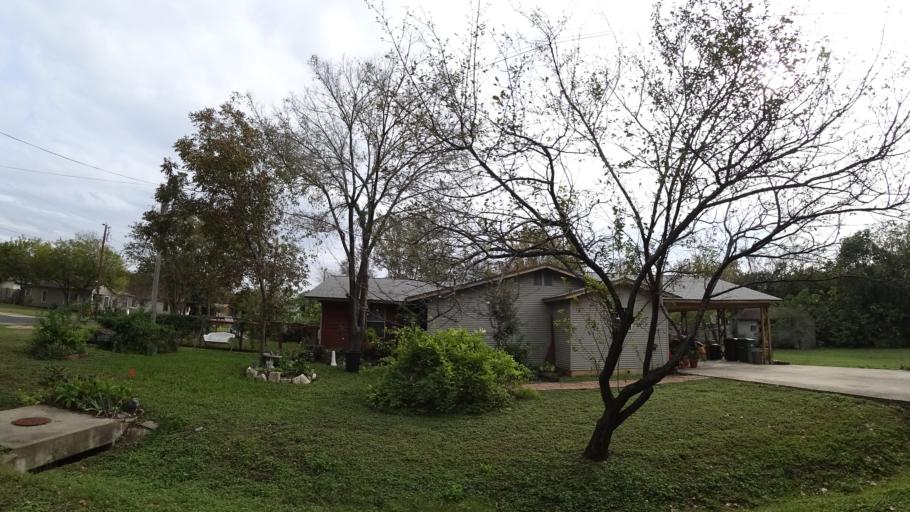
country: US
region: Texas
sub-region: Williamson County
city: Round Rock
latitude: 30.5131
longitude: -97.6786
